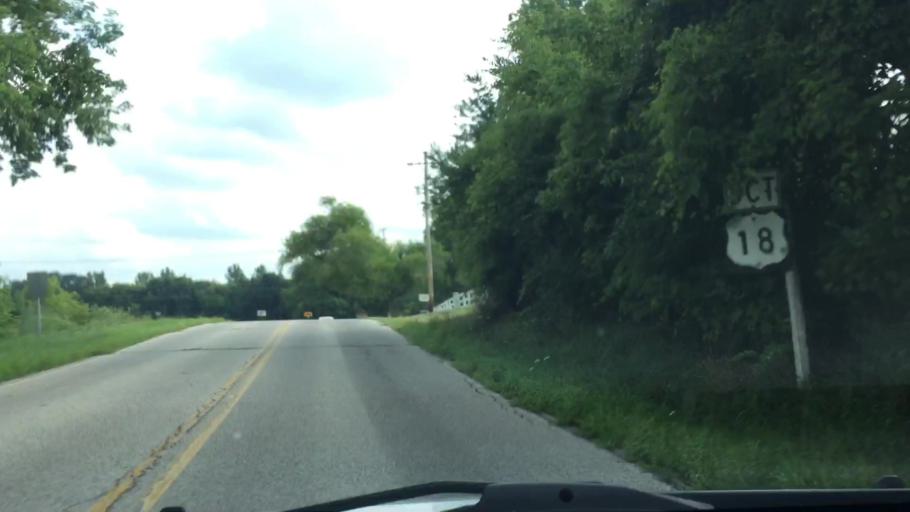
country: US
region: Wisconsin
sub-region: Waukesha County
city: Wales
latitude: 43.0201
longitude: -88.3642
